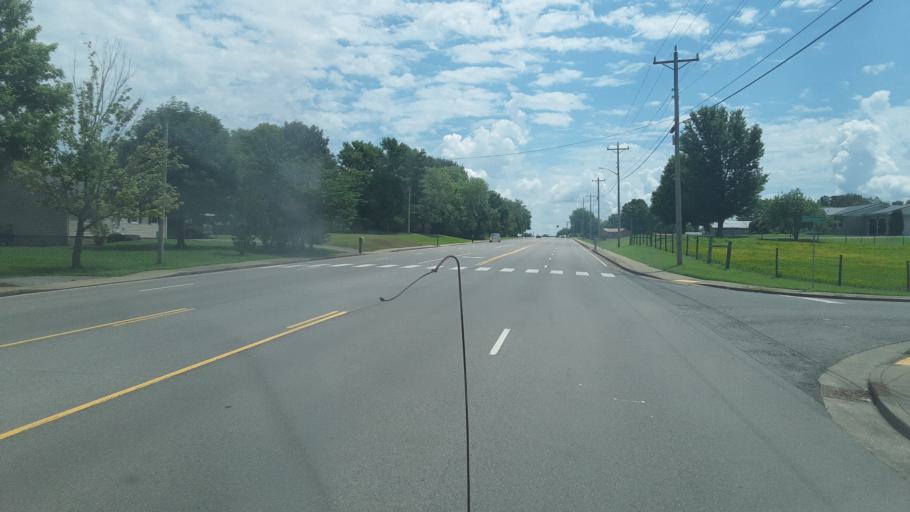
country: US
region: Kentucky
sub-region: Christian County
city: Fort Campbell North
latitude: 36.5757
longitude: -87.4405
